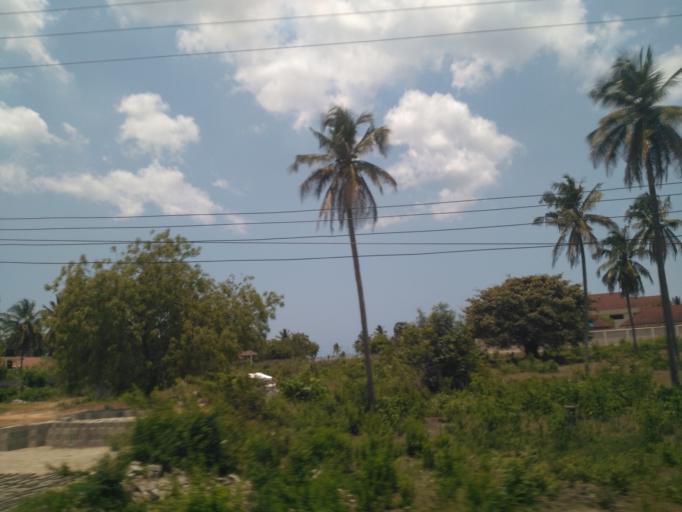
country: TZ
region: Dar es Salaam
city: Dar es Salaam
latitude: -6.8397
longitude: 39.3498
